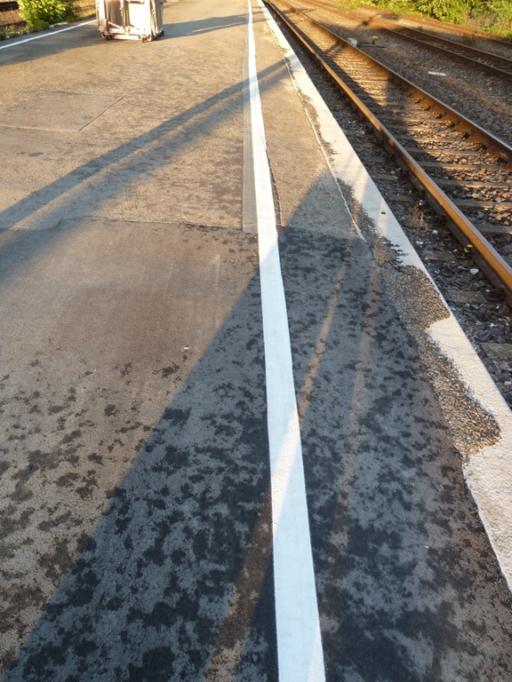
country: DE
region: Baden-Wuerttemberg
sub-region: Tuebingen Region
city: Tuebingen
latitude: 48.5155
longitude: 9.0564
